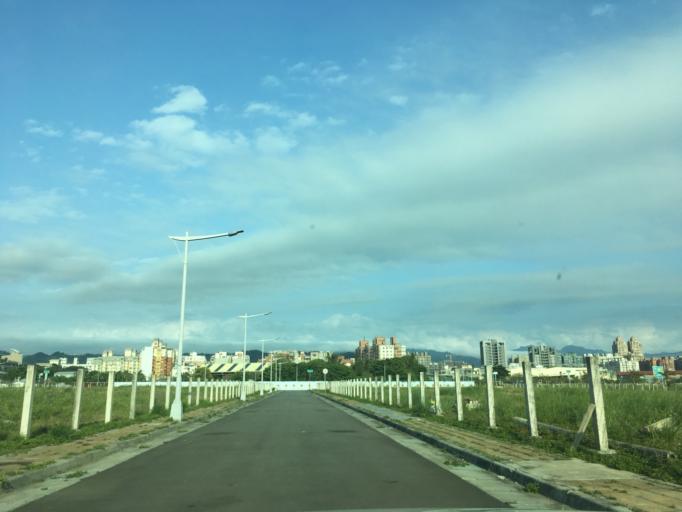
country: TW
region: Taiwan
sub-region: Taichung City
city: Taichung
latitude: 24.1948
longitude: 120.6907
